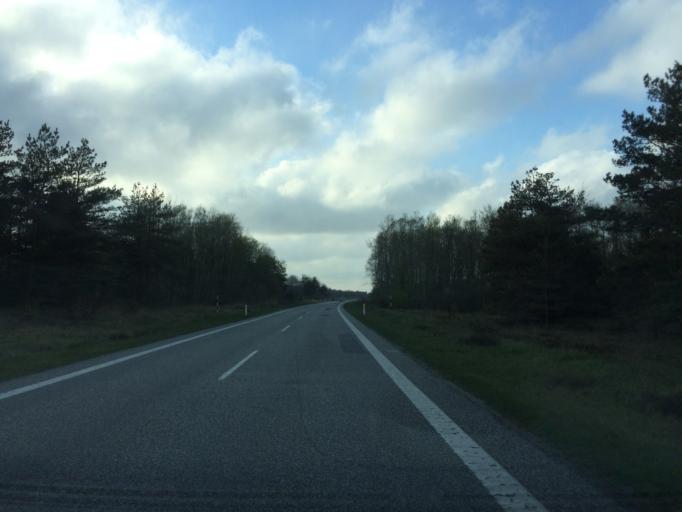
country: DK
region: Central Jutland
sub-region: Viborg Kommune
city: Karup
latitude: 56.3141
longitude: 9.1233
